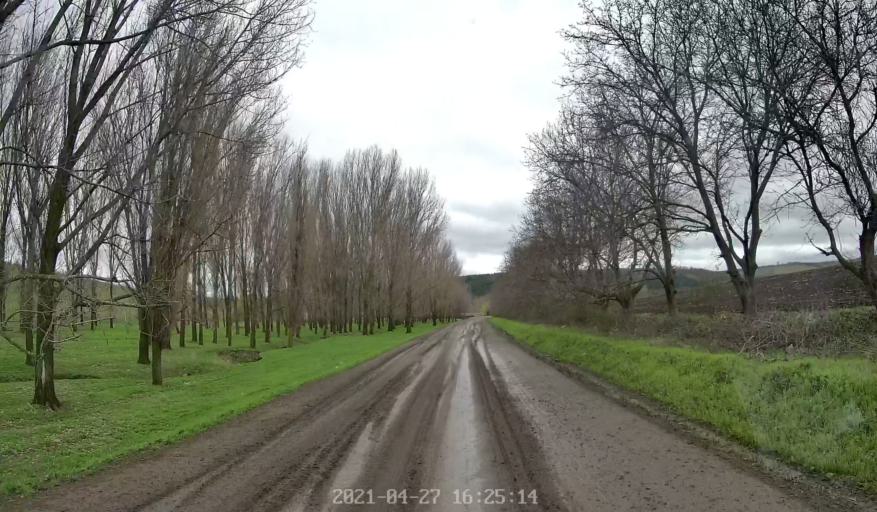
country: MD
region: Chisinau
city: Singera
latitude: 46.9863
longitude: 29.0221
